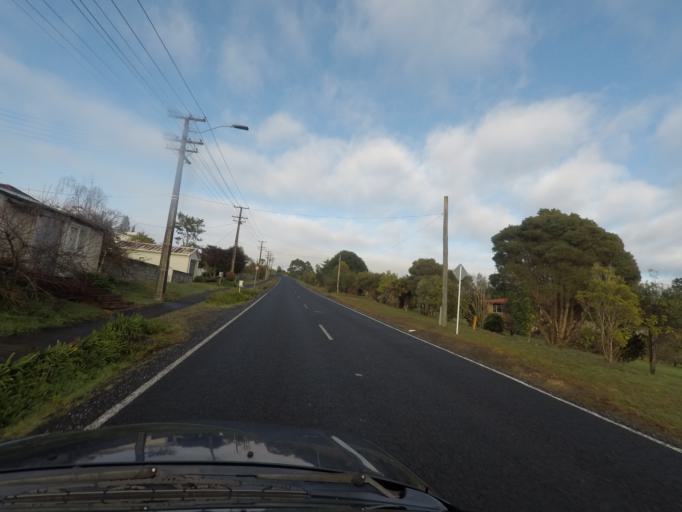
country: NZ
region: Auckland
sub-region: Auckland
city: Waitakere
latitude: -36.9011
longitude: 174.6141
